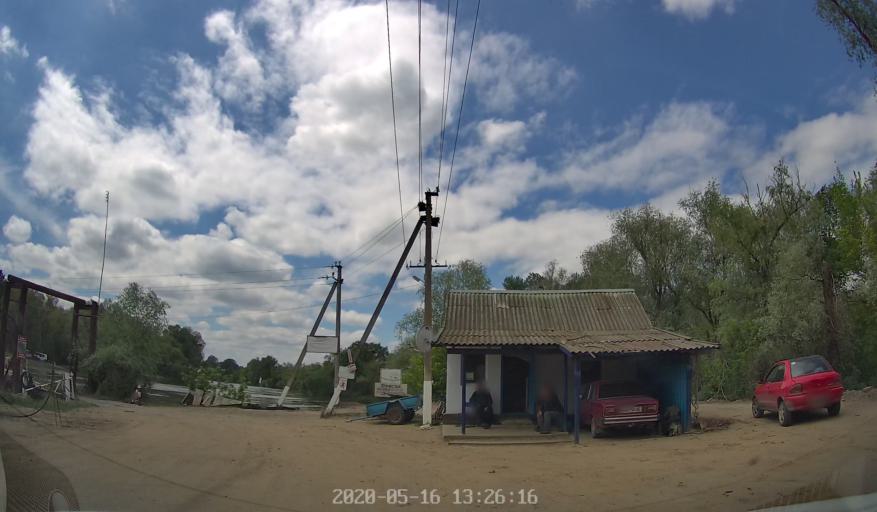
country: MD
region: Telenesti
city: Dnestrovsc
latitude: 46.5469
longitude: 30.0003
